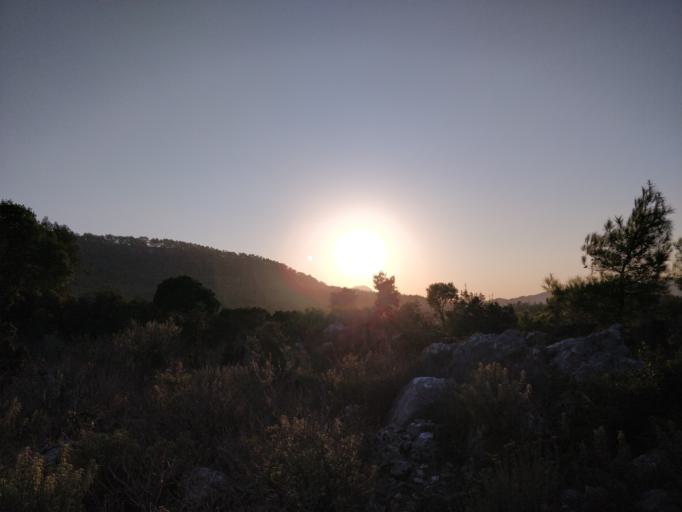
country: GR
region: South Aegean
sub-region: Nomos Dodekanisou
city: Archangelos
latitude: 36.2636
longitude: 28.0751
